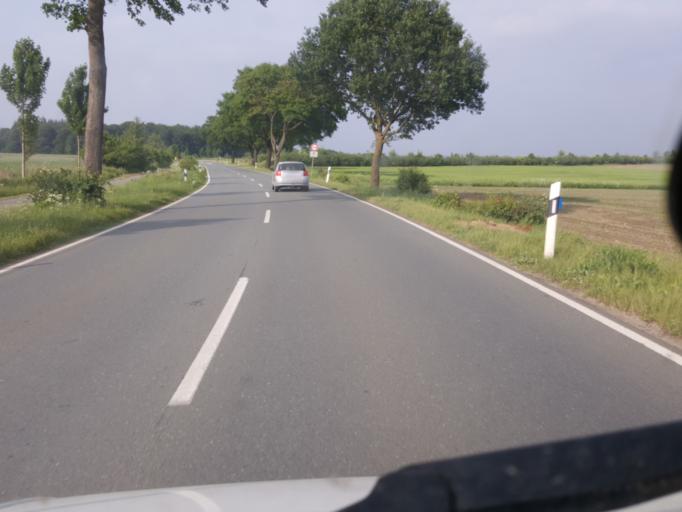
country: DE
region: Lower Saxony
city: Binnen
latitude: 52.6340
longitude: 9.1344
